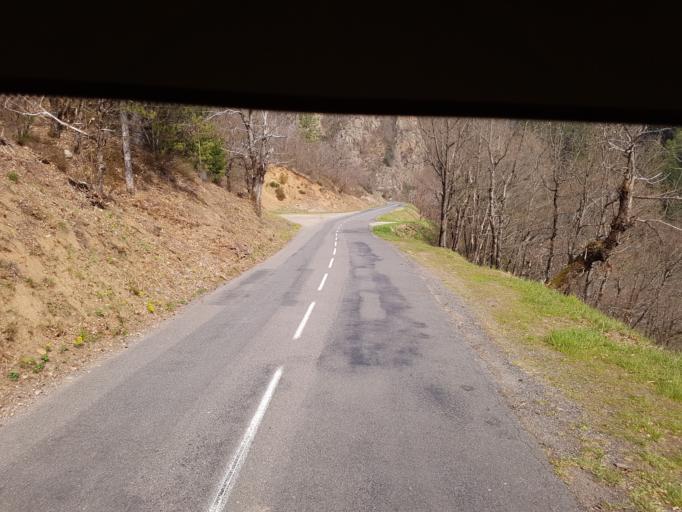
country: FR
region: Languedoc-Roussillon
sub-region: Departement de la Lozere
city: Florac
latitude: 44.3492
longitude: 3.6286
